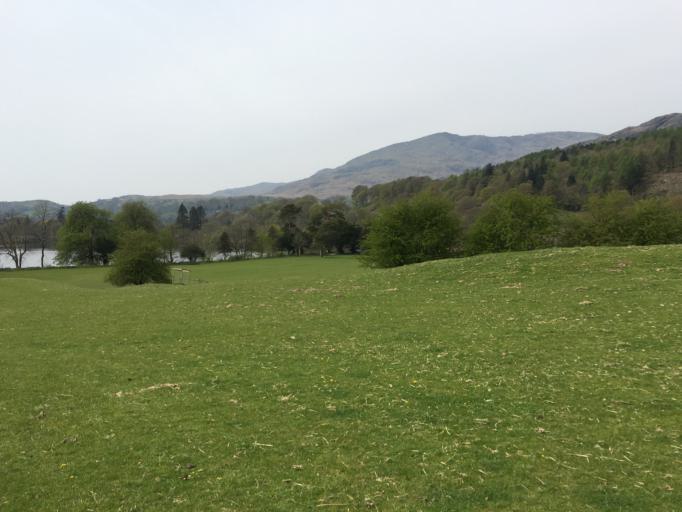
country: GB
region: England
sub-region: Cumbria
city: Ambleside
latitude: 54.3732
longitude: -3.0527
